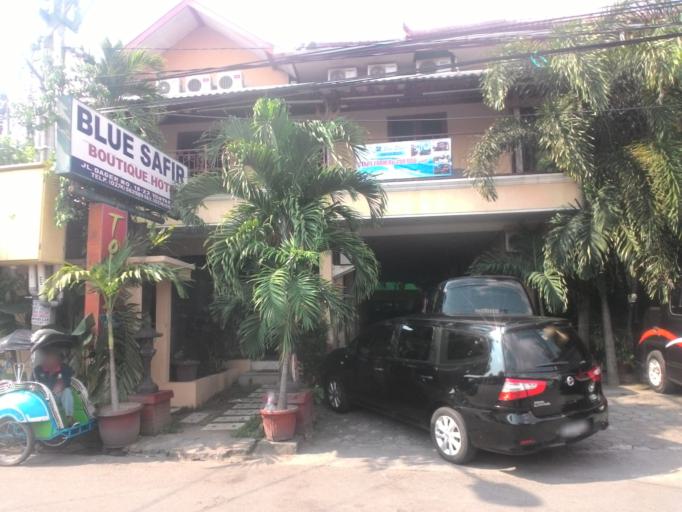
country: ID
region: Daerah Istimewa Yogyakarta
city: Yogyakarta
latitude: -7.7938
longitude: 110.3640
